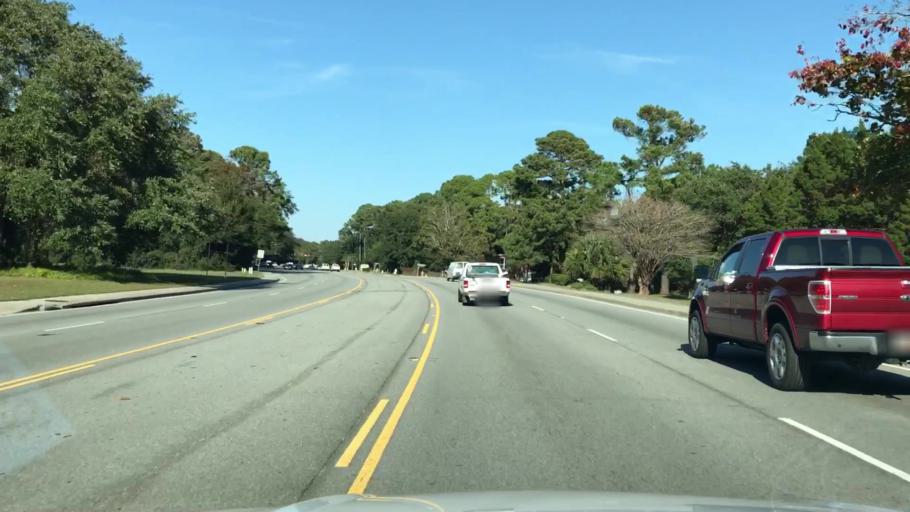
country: US
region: South Carolina
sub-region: Beaufort County
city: Hilton Head Island
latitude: 32.1989
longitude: -80.7000
